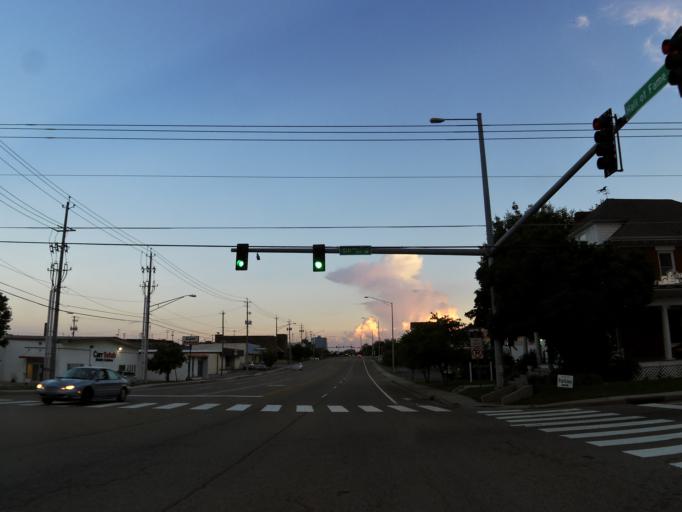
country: US
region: Tennessee
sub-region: Knox County
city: Knoxville
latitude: 35.9793
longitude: -83.9166
